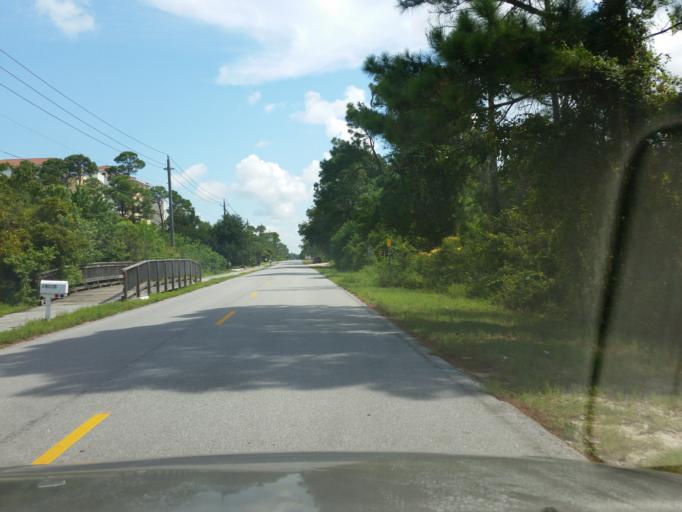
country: US
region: Alabama
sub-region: Baldwin County
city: Orange Beach
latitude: 30.2984
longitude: -87.4483
